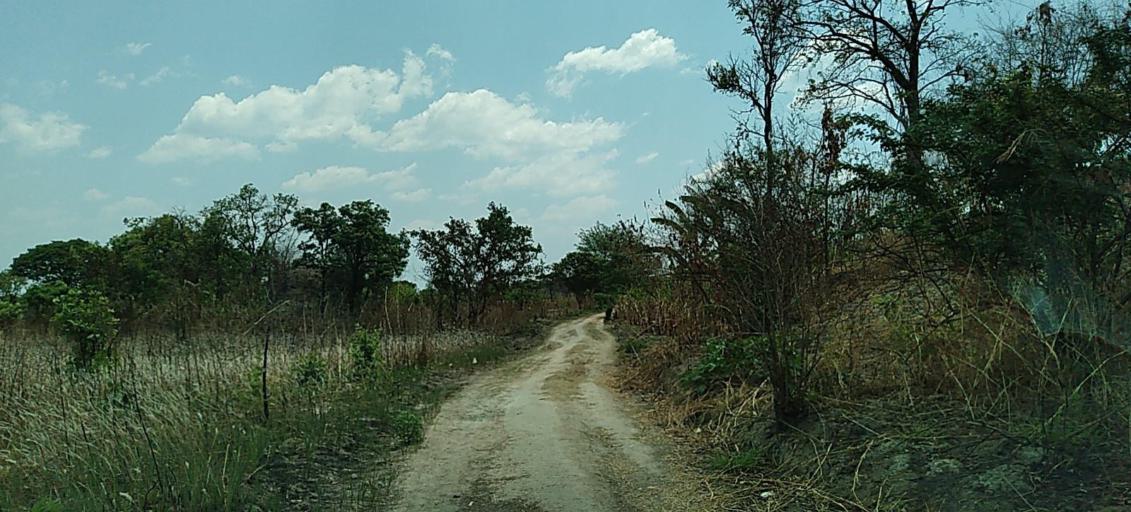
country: ZM
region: Copperbelt
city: Chililabombwe
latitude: -12.4625
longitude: 27.6691
